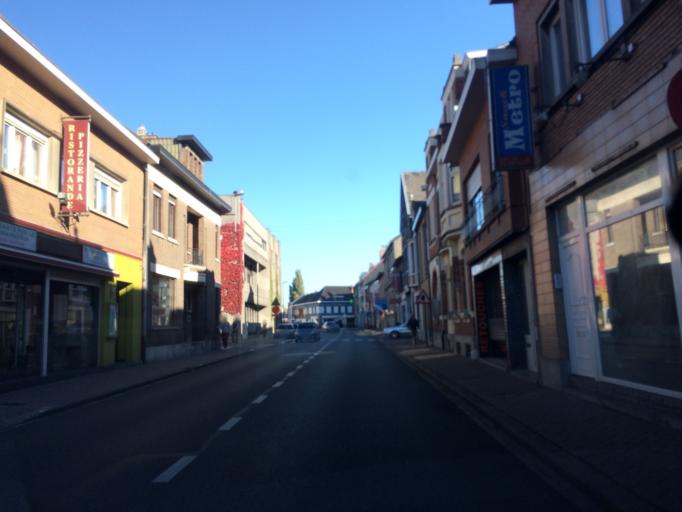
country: BE
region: Flanders
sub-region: Provincie Vlaams-Brabant
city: Merchtem
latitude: 50.9576
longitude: 4.2322
